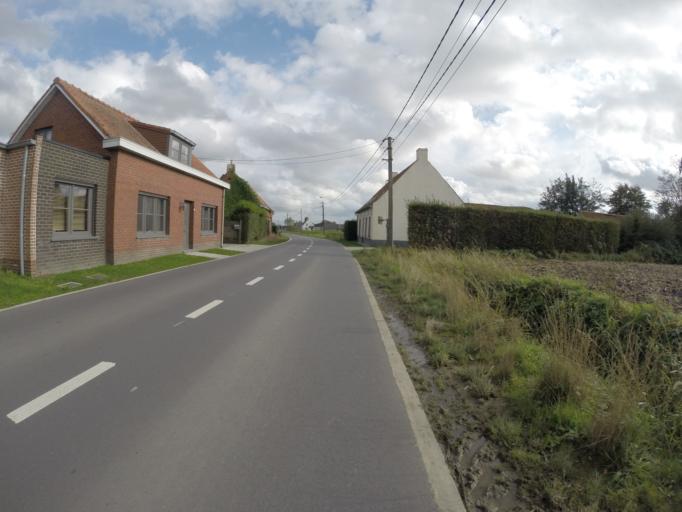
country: BE
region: Flanders
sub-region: Provincie Oost-Vlaanderen
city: Aalter
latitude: 51.0750
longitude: 3.4211
